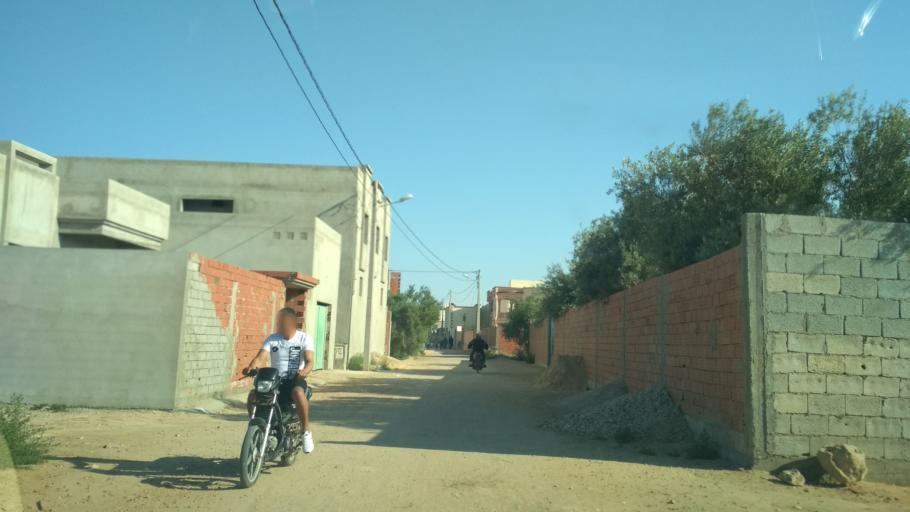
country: TN
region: Qabis
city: Gabes
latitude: 33.9515
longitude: 10.0636
